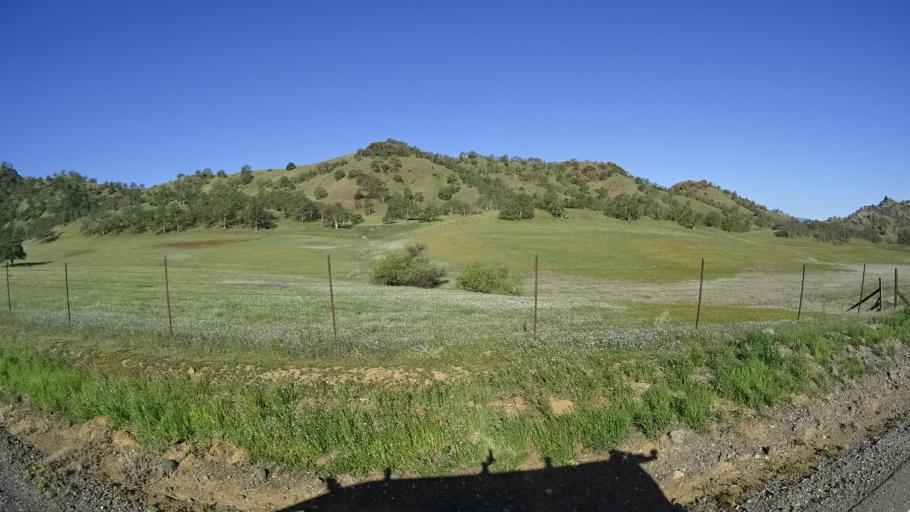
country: US
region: California
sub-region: Tehama County
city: Rancho Tehama Reserve
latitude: 39.7831
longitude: -122.5196
